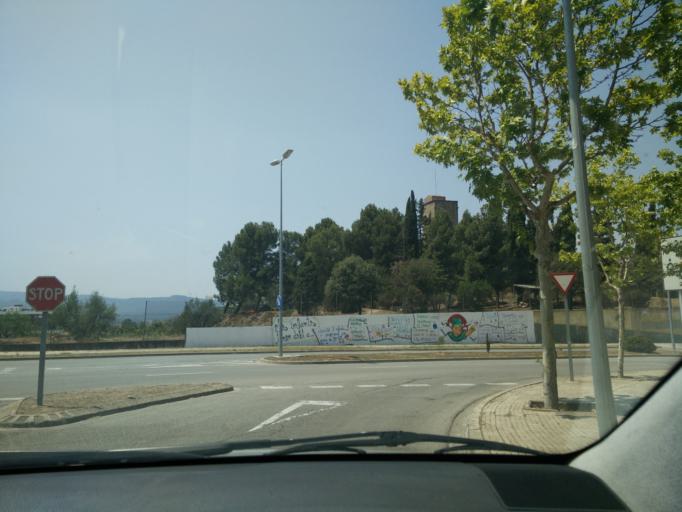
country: ES
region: Catalonia
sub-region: Provincia de Barcelona
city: Manresa
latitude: 41.7202
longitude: 1.8409
